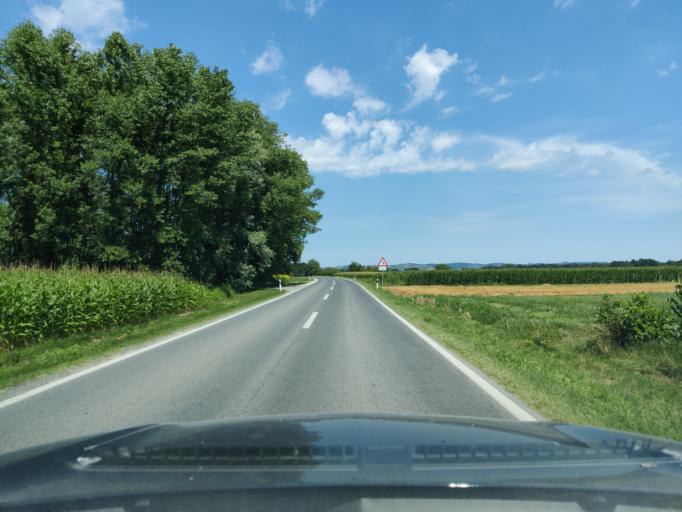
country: HR
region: Medimurska
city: Vratisinec
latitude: 46.4847
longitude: 16.4250
